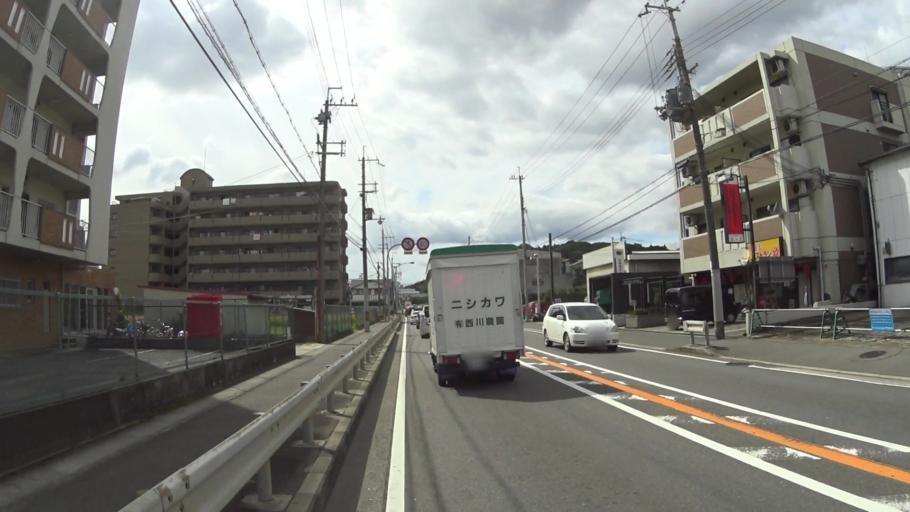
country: JP
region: Kyoto
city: Uji
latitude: 34.9320
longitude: 135.7869
